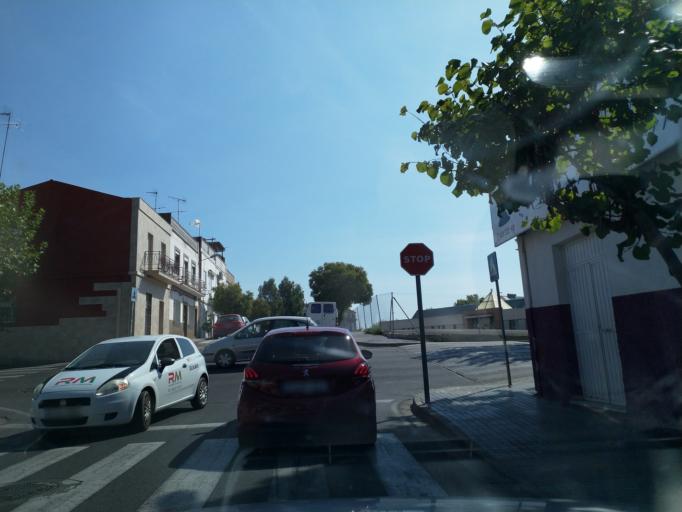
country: ES
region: Extremadura
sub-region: Provincia de Badajoz
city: Merida
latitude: 38.9184
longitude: -6.3363
